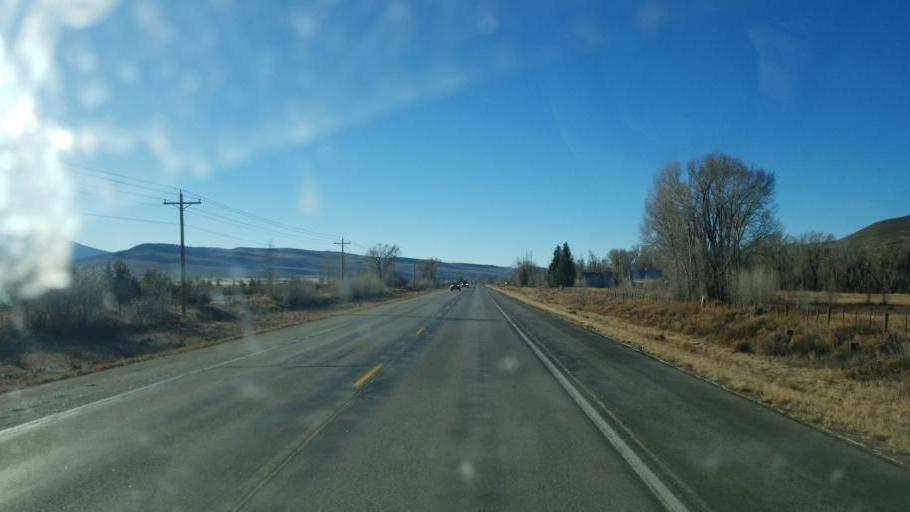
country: US
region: Colorado
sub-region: Gunnison County
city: Crested Butte
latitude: 38.7642
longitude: -106.8643
